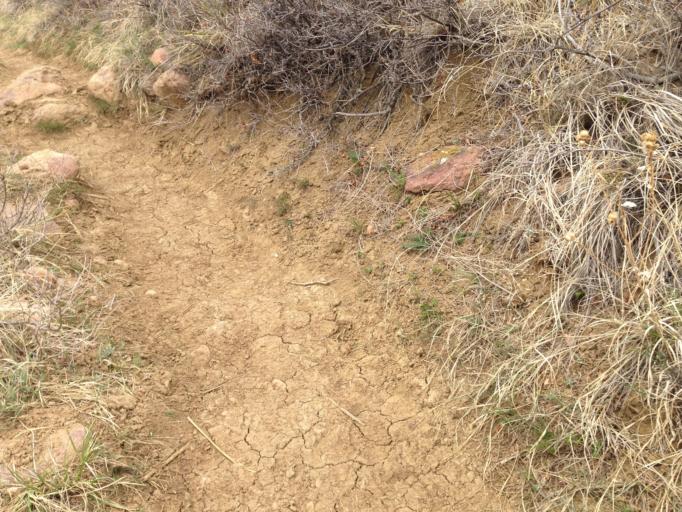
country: US
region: Colorado
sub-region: Boulder County
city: Boulder
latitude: 39.9431
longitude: -105.2696
